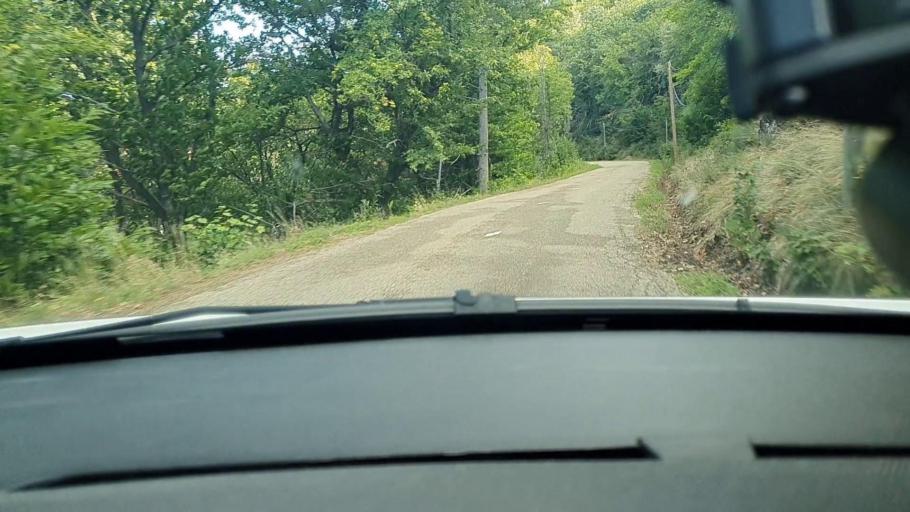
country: FR
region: Rhone-Alpes
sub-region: Departement de l'Ardeche
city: Les Vans
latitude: 44.4193
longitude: 4.0218
